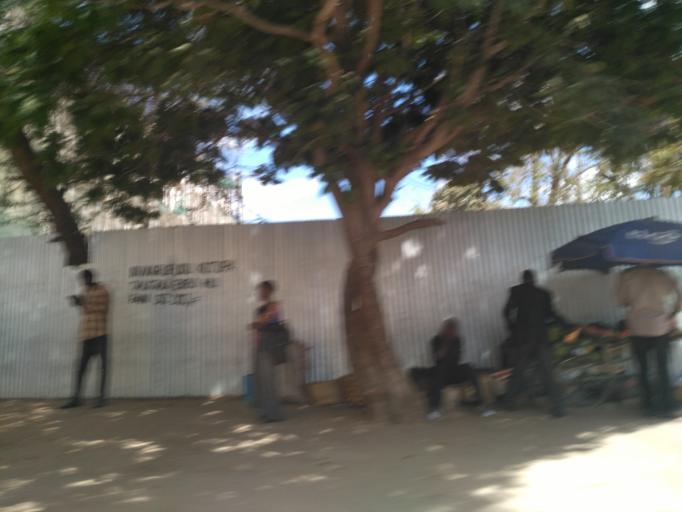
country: TZ
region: Dodoma
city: Dodoma
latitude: -6.1842
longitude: 35.7479
